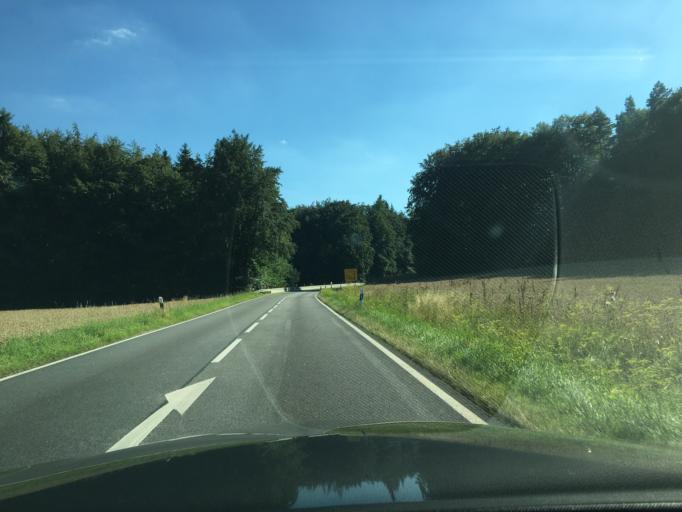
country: DE
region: Bavaria
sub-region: Upper Franconia
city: Hiltpoltstein
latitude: 49.6625
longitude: 11.3453
